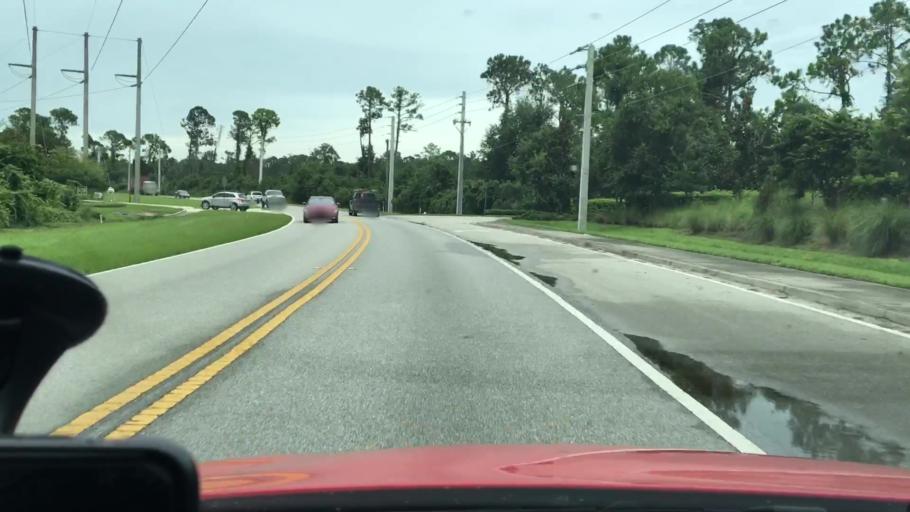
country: US
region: Florida
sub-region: Flagler County
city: Palm Coast
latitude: 29.5492
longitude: -81.2143
